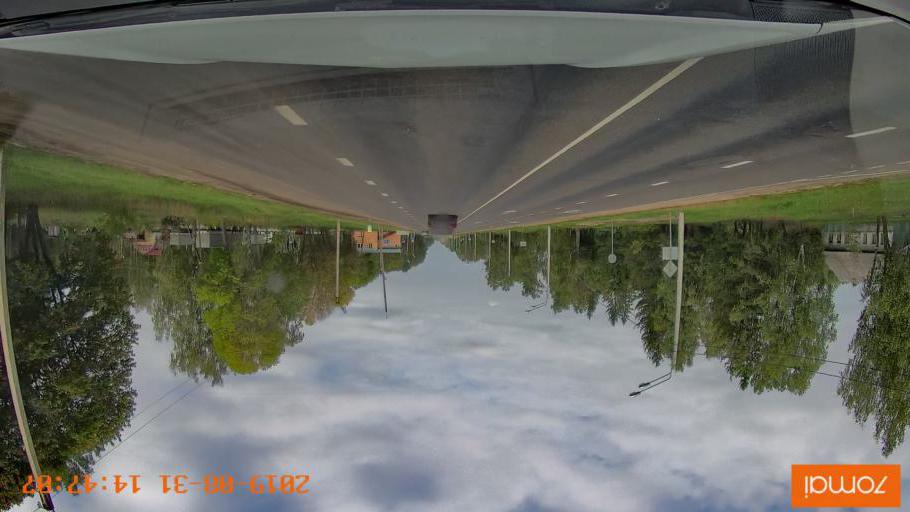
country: RU
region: Kaluga
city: Betlitsa
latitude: 54.2376
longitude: 33.7210
